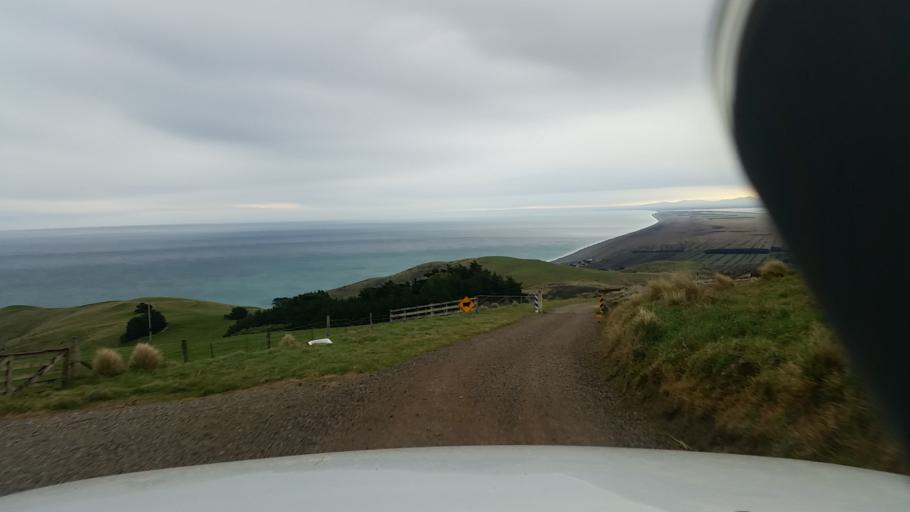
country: NZ
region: Canterbury
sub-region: Christchurch City
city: Christchurch
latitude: -43.8172
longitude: 172.7489
